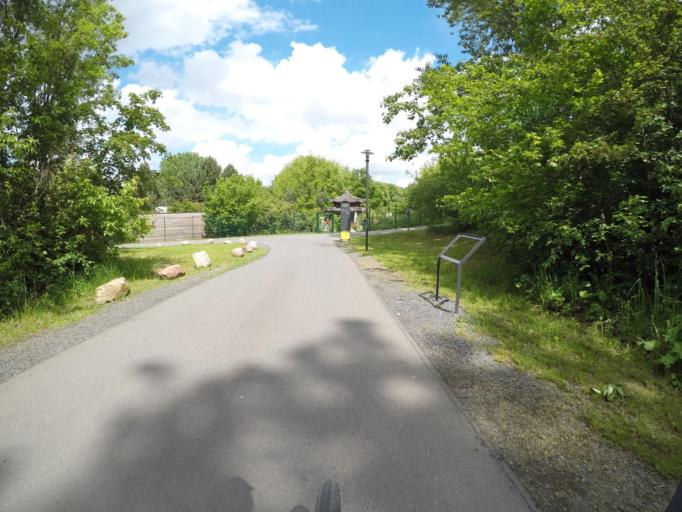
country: DE
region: Berlin
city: Marzahn
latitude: 52.5357
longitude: 13.5770
